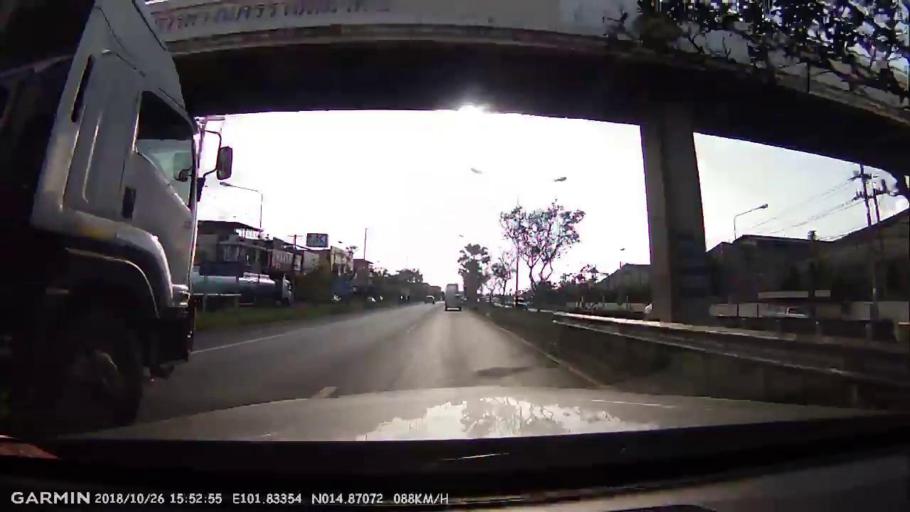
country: TH
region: Nakhon Ratchasima
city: Sung Noen
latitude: 14.8707
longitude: 101.8334
